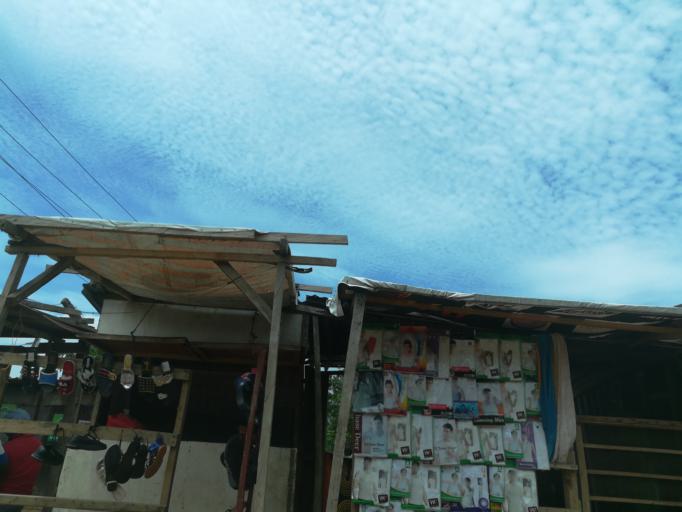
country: NG
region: Lagos
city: Ebute Ikorodu
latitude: 6.5768
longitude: 3.4888
